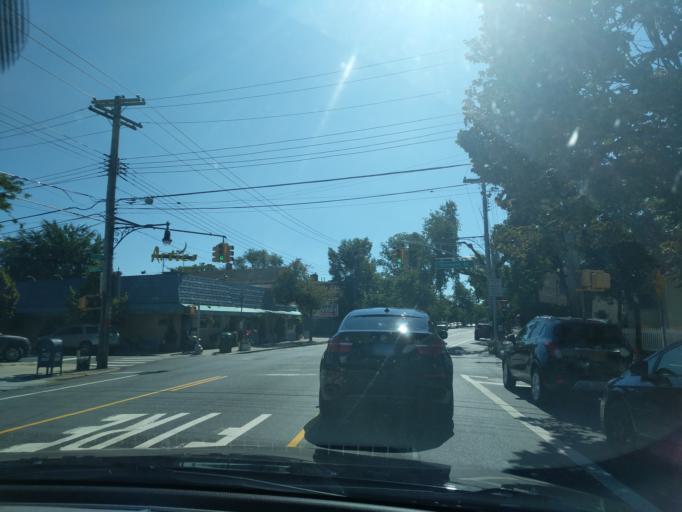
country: US
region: New York
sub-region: Westchester County
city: Pelham Manor
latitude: 40.8498
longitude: -73.7876
